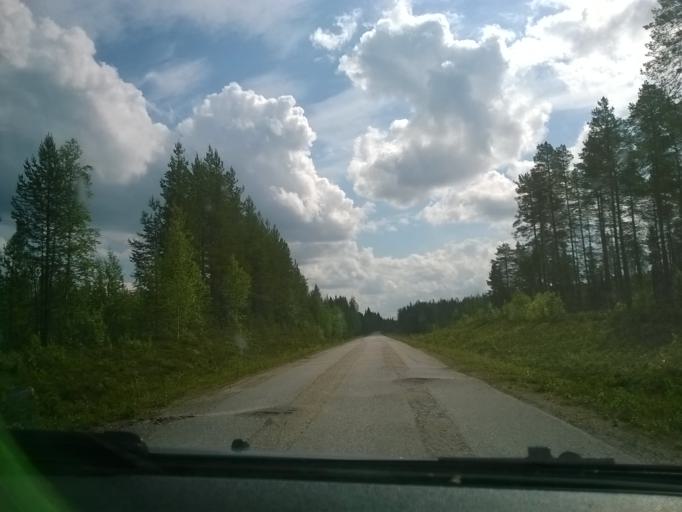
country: FI
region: Kainuu
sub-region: Kehys-Kainuu
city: Kuhmo
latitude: 64.4244
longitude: 29.7468
